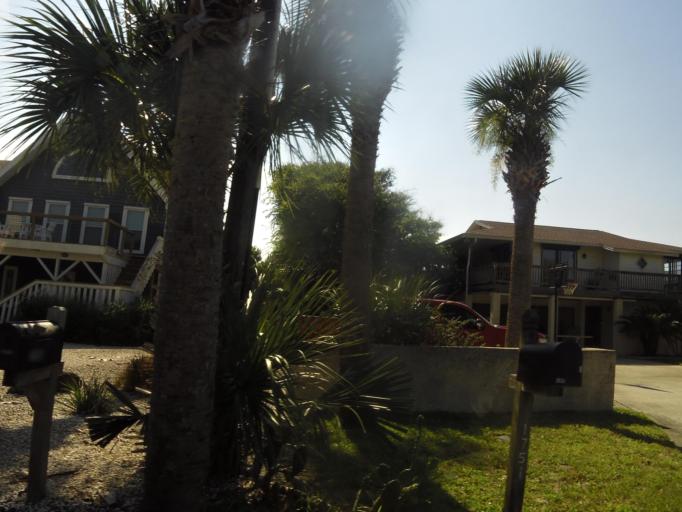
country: US
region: Florida
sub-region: Nassau County
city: Fernandina Beach
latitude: 30.6907
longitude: -81.4311
